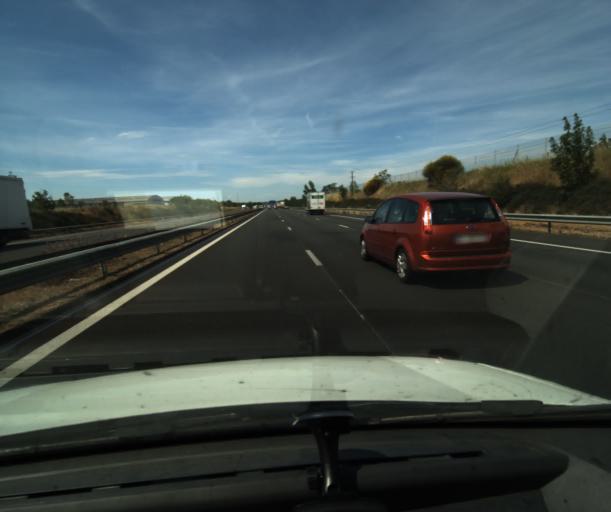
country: FR
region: Midi-Pyrenees
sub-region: Departement de la Haute-Garonne
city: Saint-Alban
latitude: 43.7074
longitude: 1.4048
